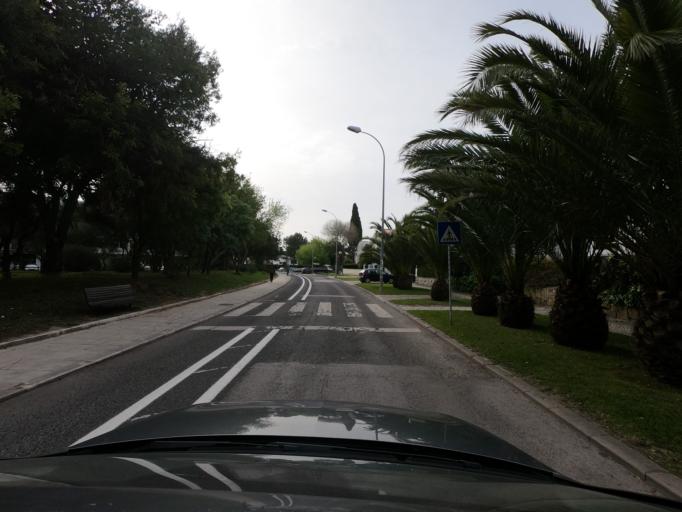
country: PT
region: Lisbon
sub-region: Oeiras
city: Carcavelos
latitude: 38.6906
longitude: -9.3233
